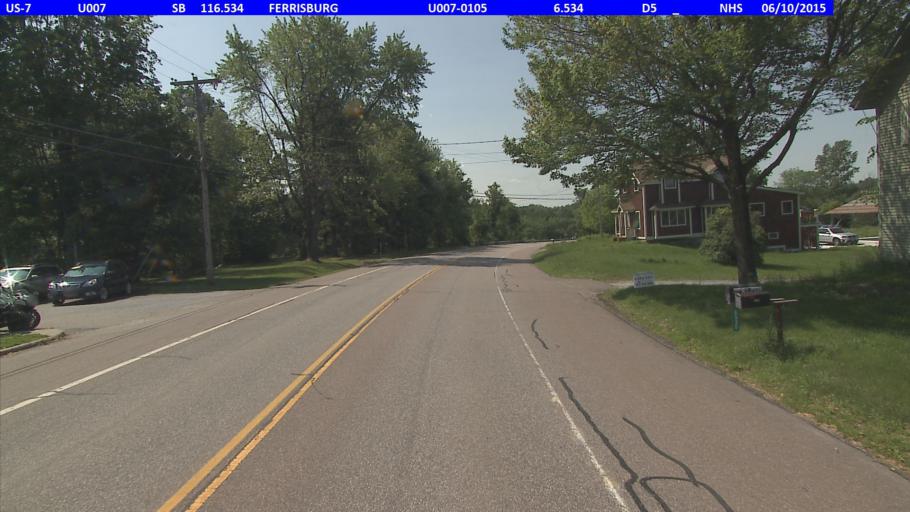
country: US
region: Vermont
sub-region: Addison County
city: Vergennes
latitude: 44.2530
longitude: -73.2275
